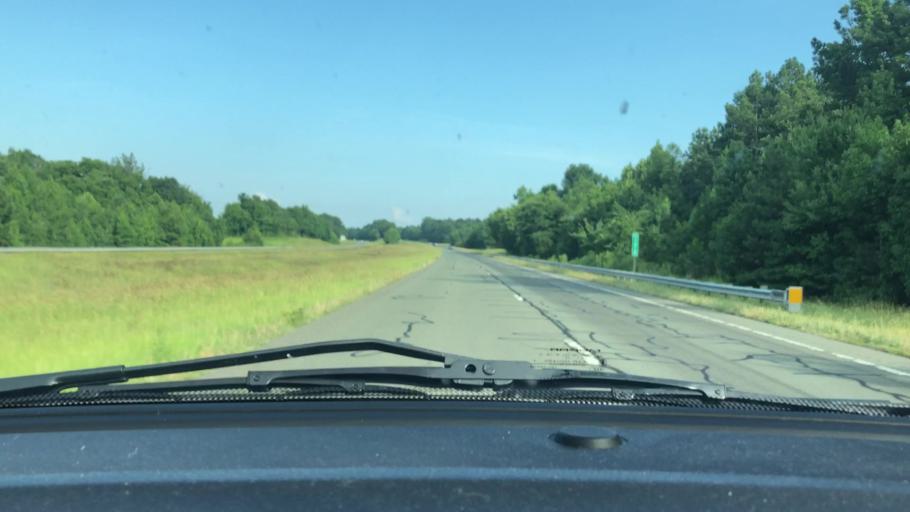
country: US
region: North Carolina
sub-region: Randolph County
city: Liberty
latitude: 35.7947
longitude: -79.5321
